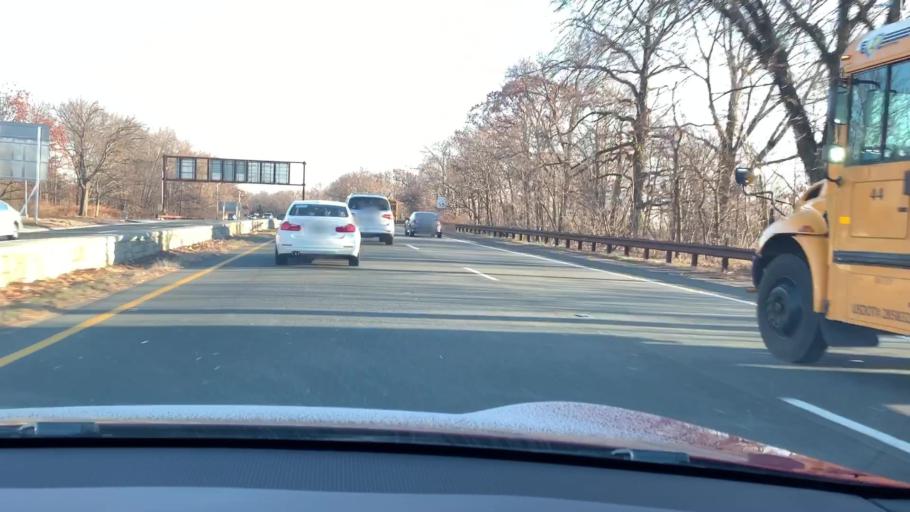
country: US
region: New Jersey
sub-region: Bergen County
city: Fort Lee
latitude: 40.8619
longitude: -73.9571
